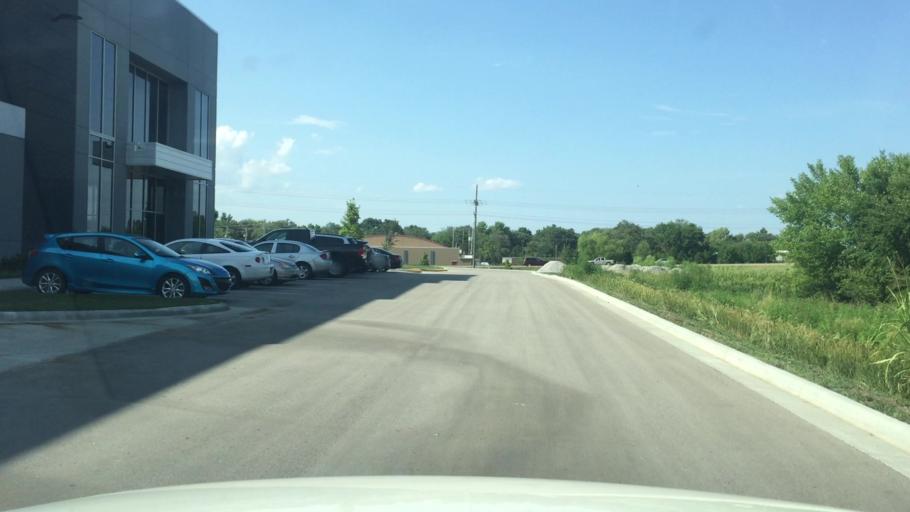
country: US
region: Kansas
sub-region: Johnson County
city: Olathe
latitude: 38.8661
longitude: -94.8283
